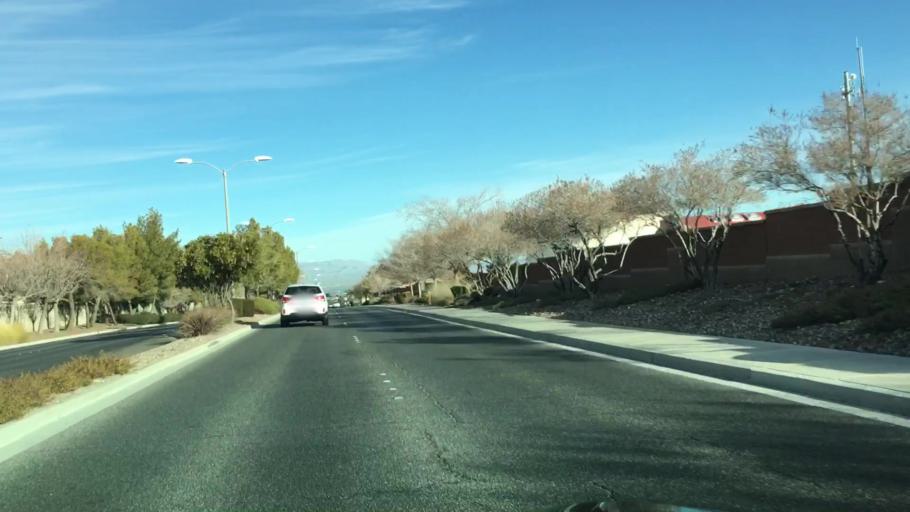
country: US
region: Nevada
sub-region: Clark County
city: Whitney
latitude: 35.9762
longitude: -115.1008
